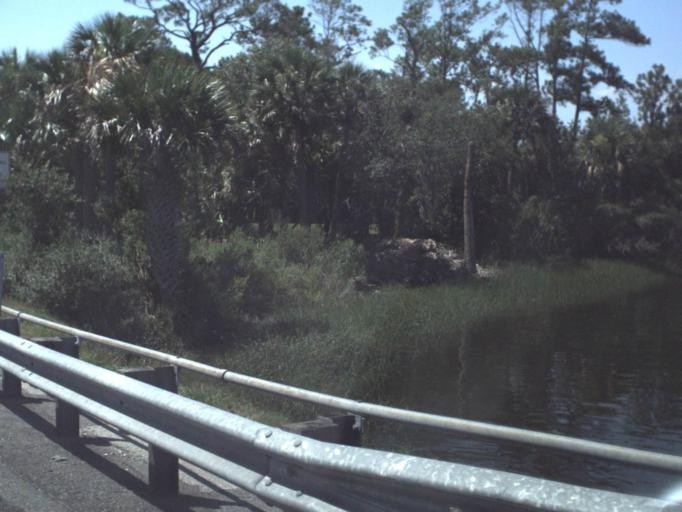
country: US
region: Florida
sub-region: Duval County
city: Atlantic Beach
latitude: 30.4045
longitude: -81.5073
